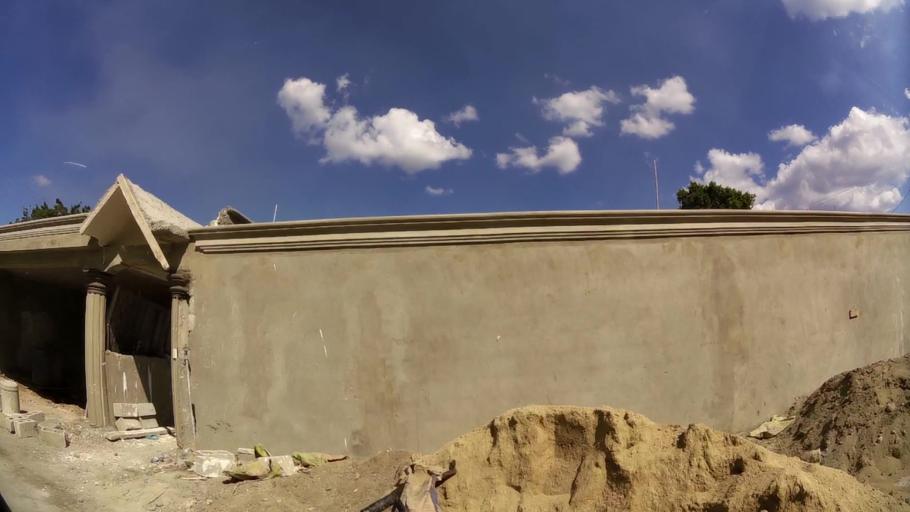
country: DO
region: Santo Domingo
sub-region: Santo Domingo
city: Santo Domingo Este
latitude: 18.4676
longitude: -69.7674
